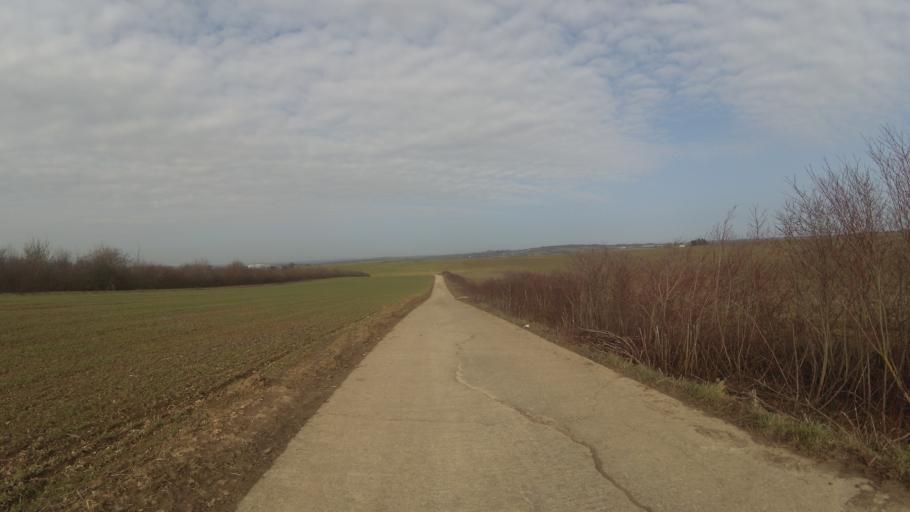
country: FR
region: Lorraine
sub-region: Departement de la Moselle
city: Merten
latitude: 49.2830
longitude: 6.6669
